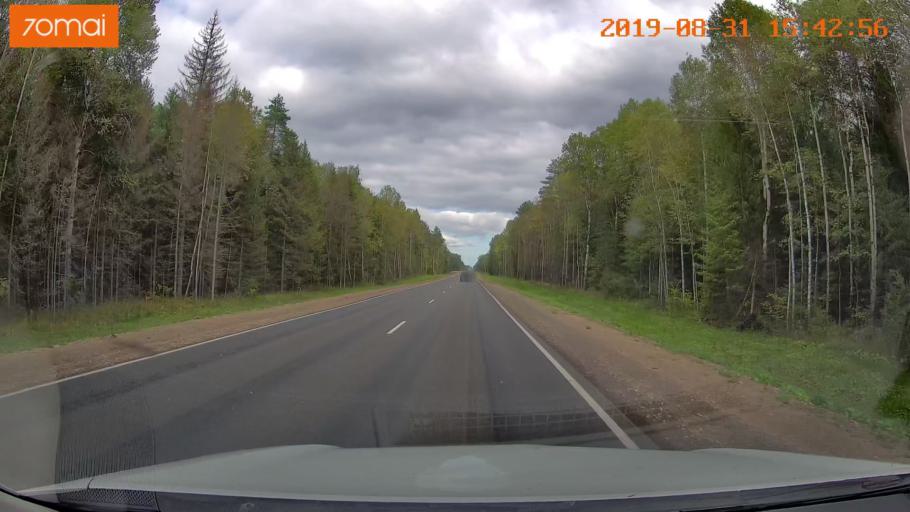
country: RU
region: Kaluga
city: Mosal'sk
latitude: 54.6496
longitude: 34.8986
